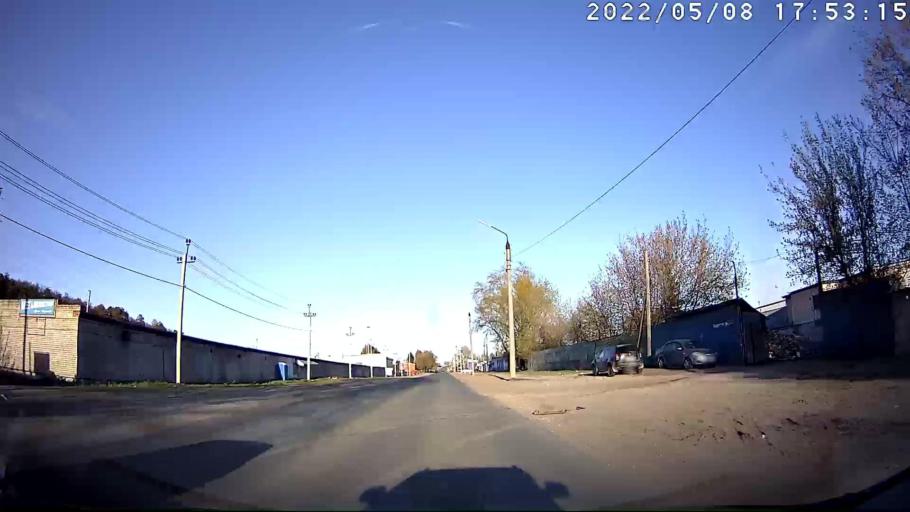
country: RU
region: Tatarstan
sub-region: Zelenodol'skiy Rayon
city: Zelenodolsk
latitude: 55.8398
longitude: 48.5150
